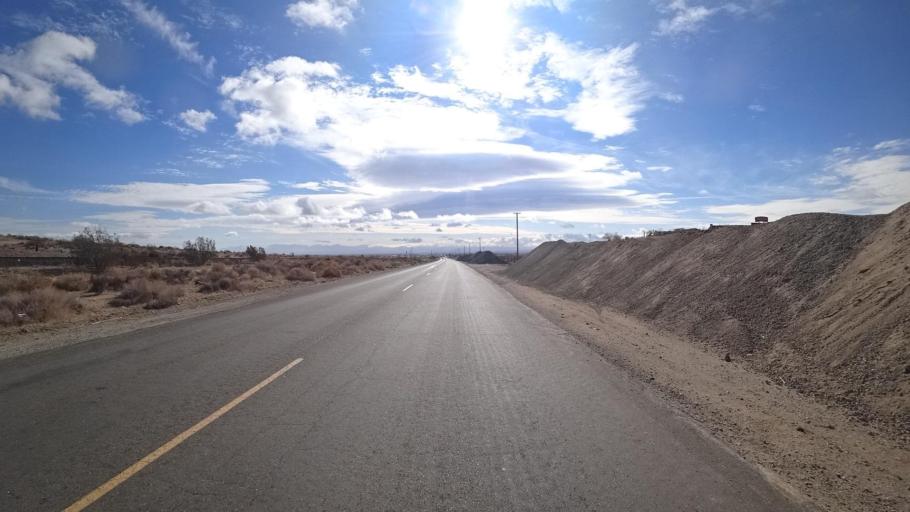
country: US
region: California
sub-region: Kern County
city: Rosamond
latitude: 34.8786
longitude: -118.1652
